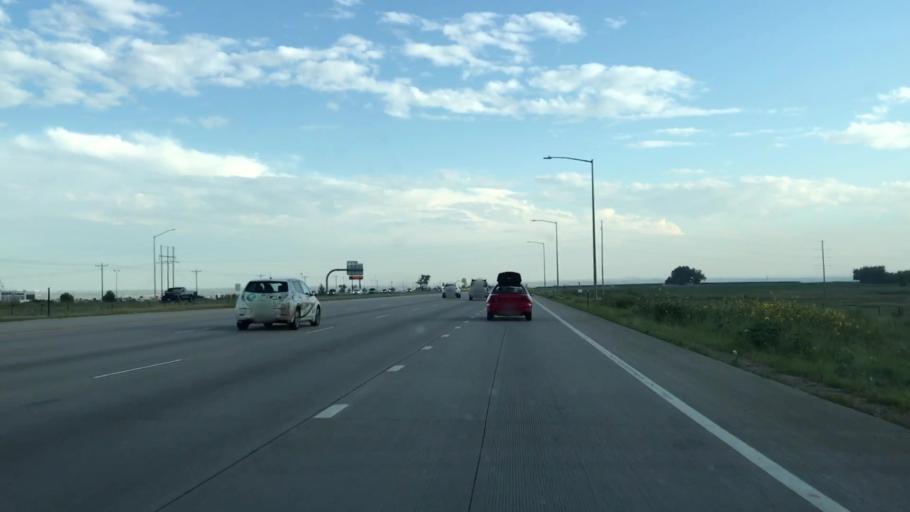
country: US
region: Colorado
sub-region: Weld County
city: Mead
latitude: 40.1993
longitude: -104.9805
